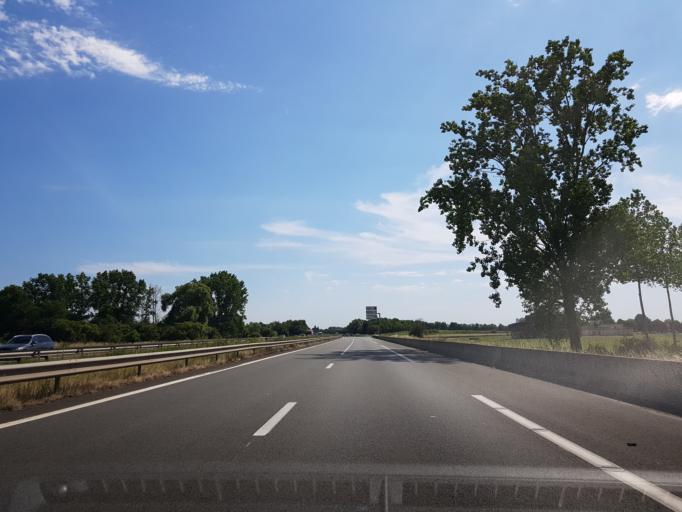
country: FR
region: Nord-Pas-de-Calais
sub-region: Departement du Nord
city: Vicq
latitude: 50.4098
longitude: 3.6229
